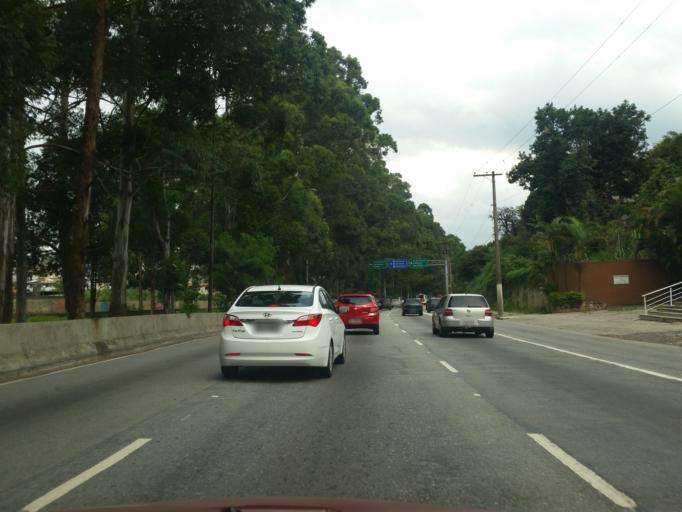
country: BR
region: Sao Paulo
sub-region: Ferraz De Vasconcelos
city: Ferraz de Vasconcelos
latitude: -23.5469
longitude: -46.4470
